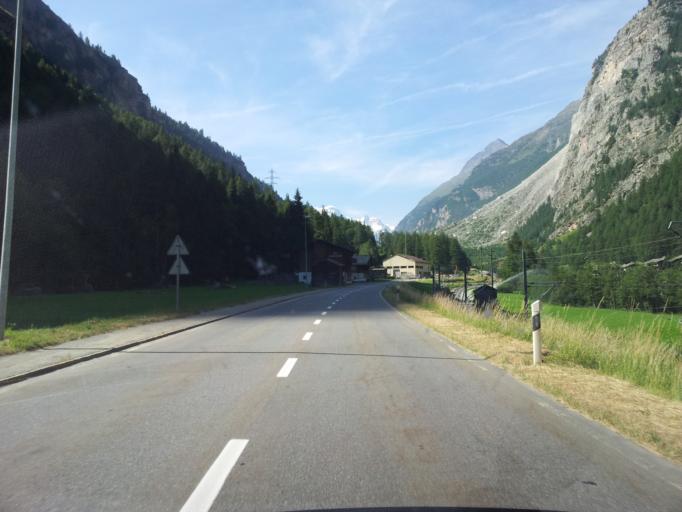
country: CH
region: Valais
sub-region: Visp District
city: Sankt Niklaus
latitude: 46.1301
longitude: 7.7924
